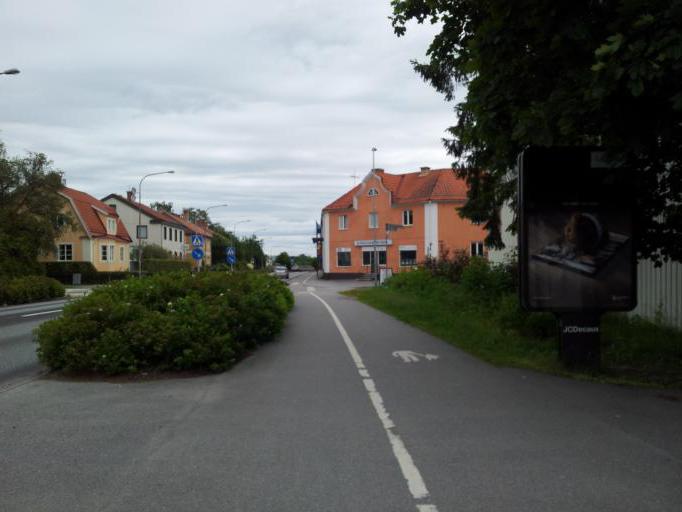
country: SE
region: Uppsala
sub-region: Uppsala Kommun
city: Uppsala
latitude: 59.8714
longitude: 17.6316
